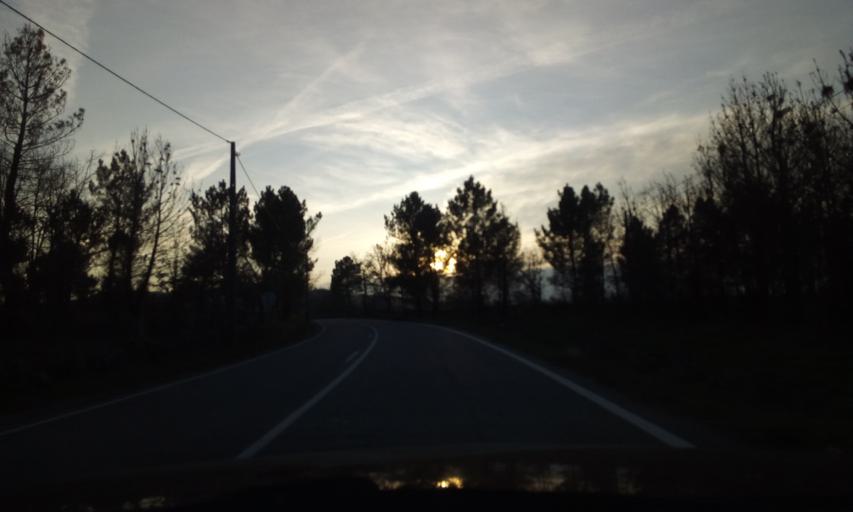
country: PT
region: Guarda
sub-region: Guarda
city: Sequeira
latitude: 40.5990
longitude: -7.1150
